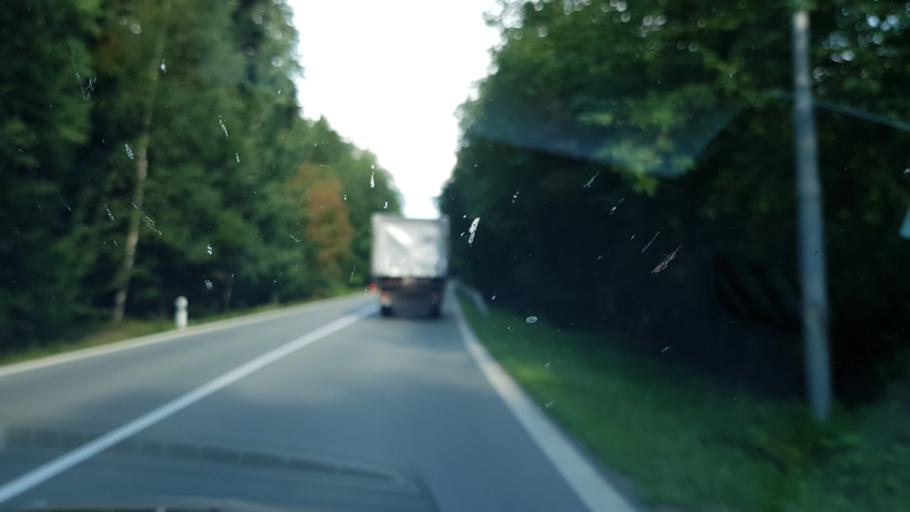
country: CZ
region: Pardubicky
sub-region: Okres Usti nad Orlici
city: Kunvald
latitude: 50.0887
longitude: 16.5545
